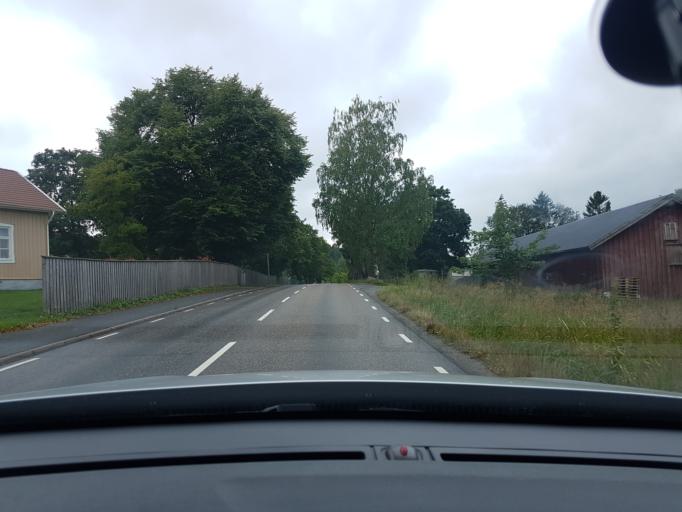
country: SE
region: Vaestra Goetaland
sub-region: Ale Kommun
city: Skepplanda
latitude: 57.9819
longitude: 12.2027
